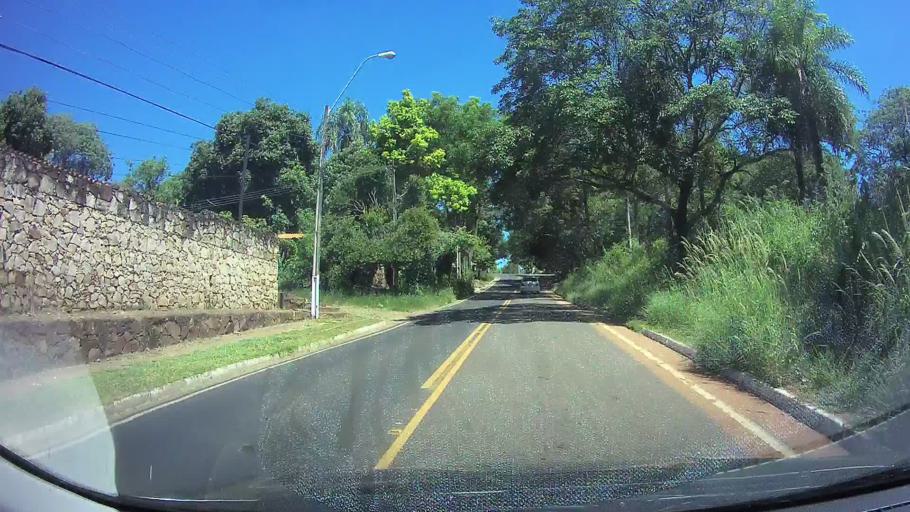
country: PY
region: Central
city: Aregua
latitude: -25.3191
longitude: -57.3893
